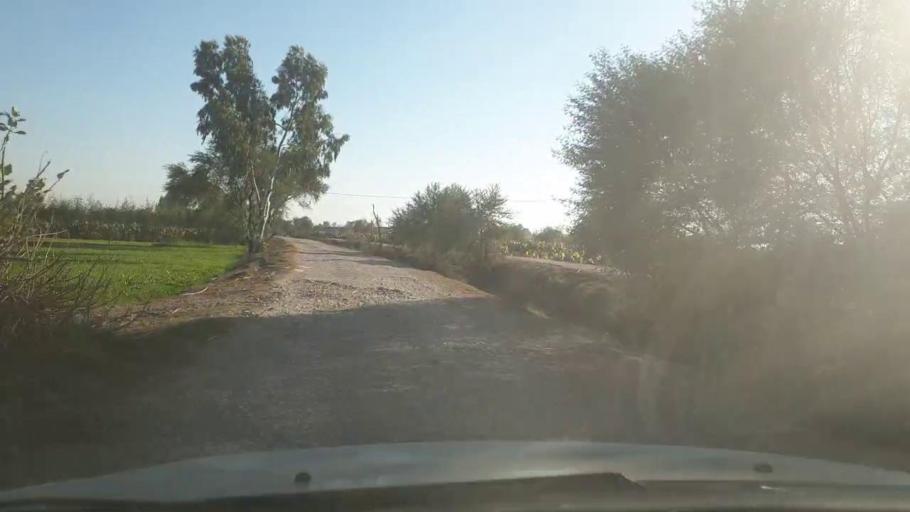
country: PK
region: Sindh
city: Adilpur
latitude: 27.9460
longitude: 69.2186
